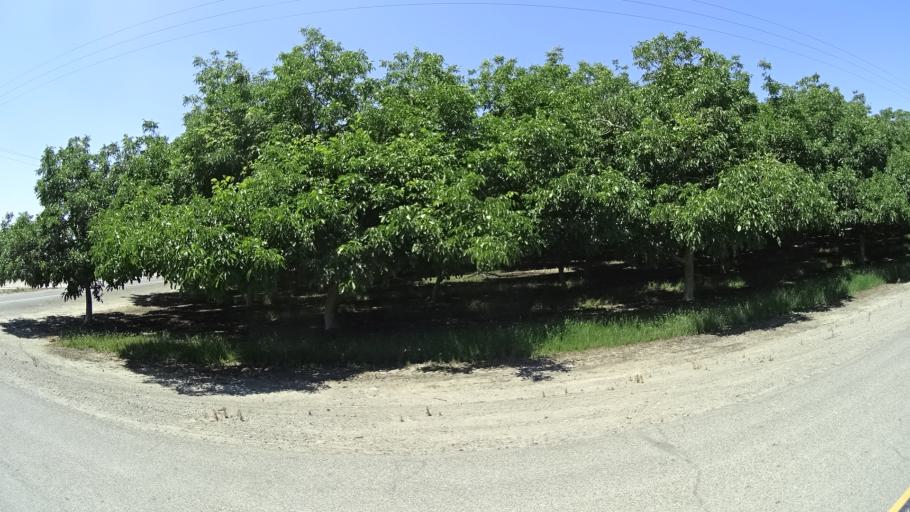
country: US
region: California
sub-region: Kings County
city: Lucerne
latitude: 36.4014
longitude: -119.6189
